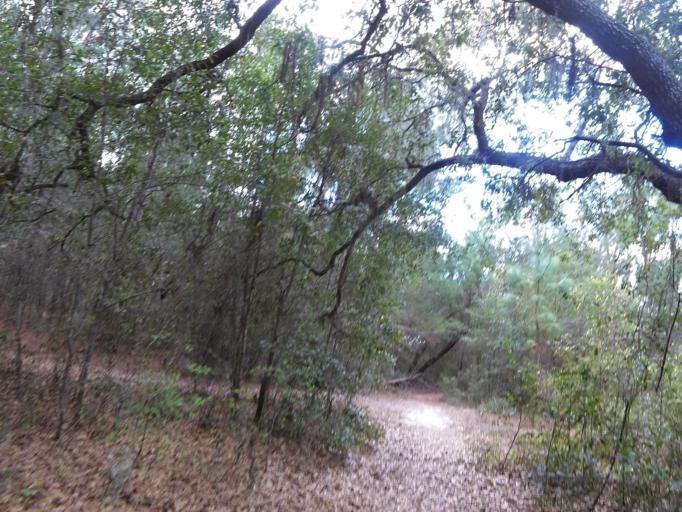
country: US
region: Florida
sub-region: Clay County
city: Keystone Heights
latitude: 29.7858
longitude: -81.8758
